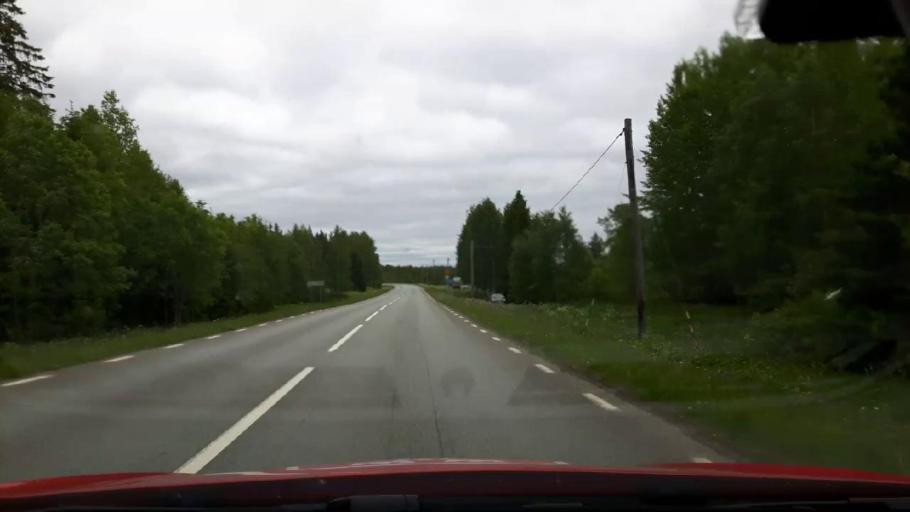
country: SE
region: Jaemtland
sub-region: Stroemsunds Kommun
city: Stroemsund
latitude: 63.5348
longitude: 15.4472
